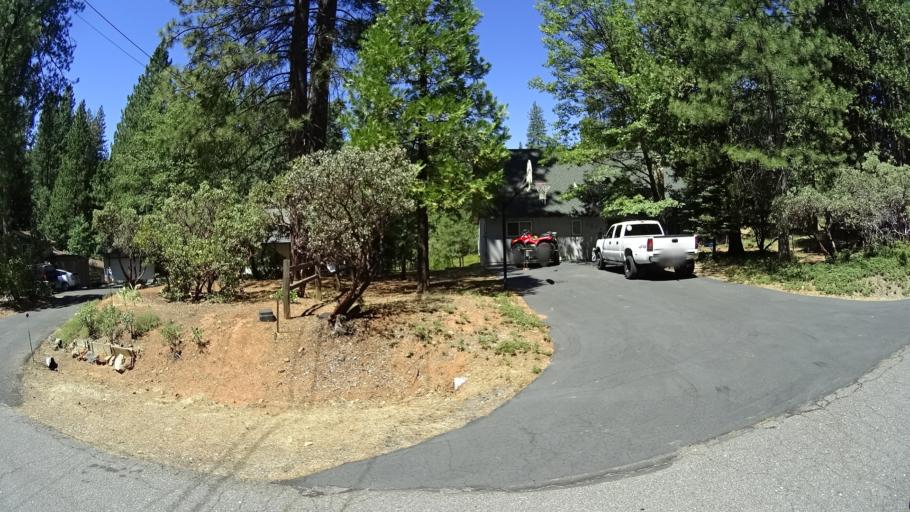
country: US
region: California
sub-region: Calaveras County
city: Arnold
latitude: 38.2282
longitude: -120.3370
